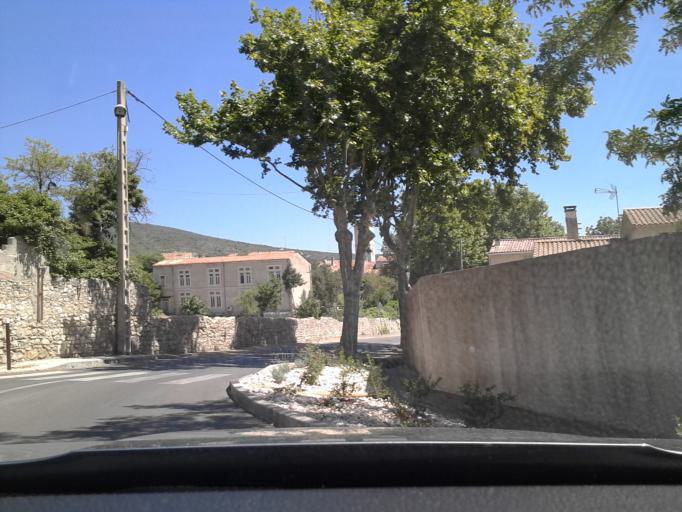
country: FR
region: Languedoc-Roussillon
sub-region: Departement de l'Herault
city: Montpeyroux
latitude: 43.6946
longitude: 3.5036
